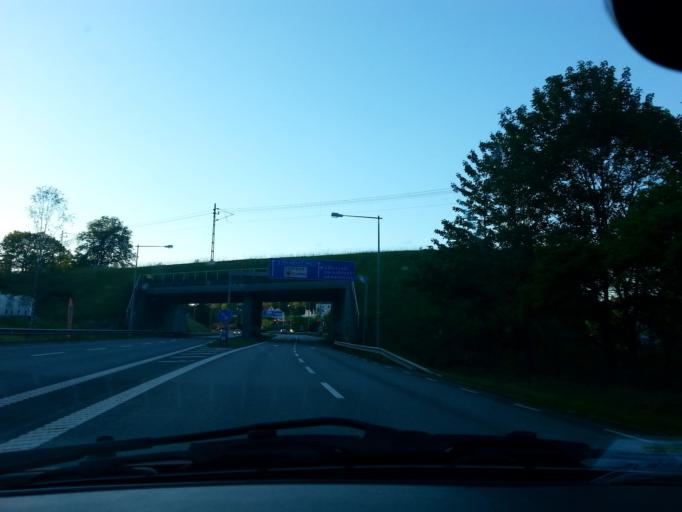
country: SE
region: Vaestra Goetaland
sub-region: Boras Kommun
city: Boras
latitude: 57.7061
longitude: 12.9498
